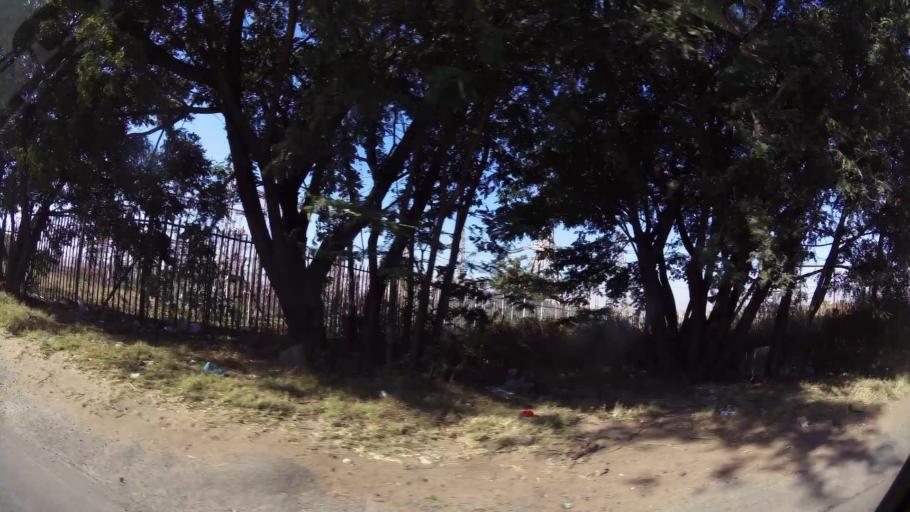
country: ZA
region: Gauteng
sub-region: Ekurhuleni Metropolitan Municipality
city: Germiston
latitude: -26.2285
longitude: 28.1134
